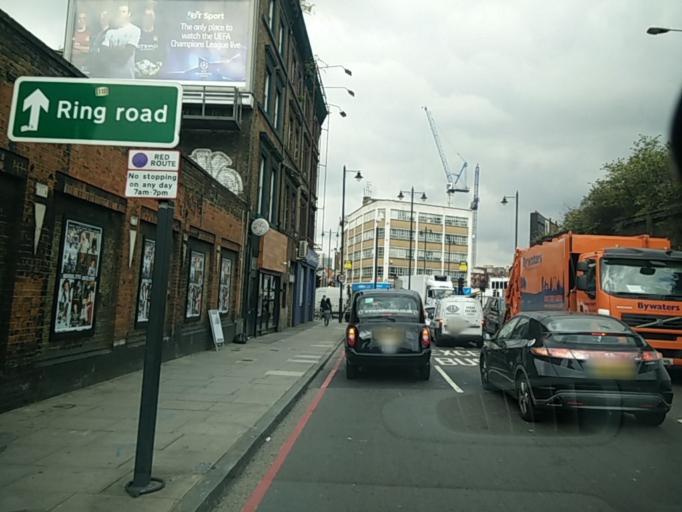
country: GB
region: England
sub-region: Greater London
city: Bethnal Green
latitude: 51.5225
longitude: -0.0770
